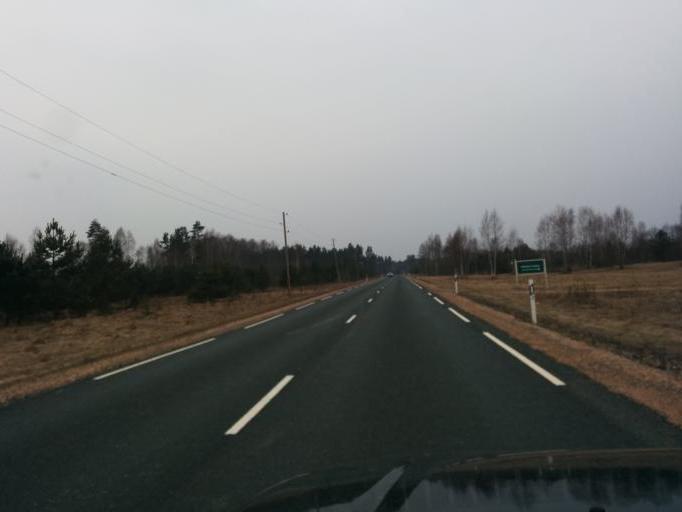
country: LV
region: Ikskile
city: Ikskile
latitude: 56.8043
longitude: 24.5537
